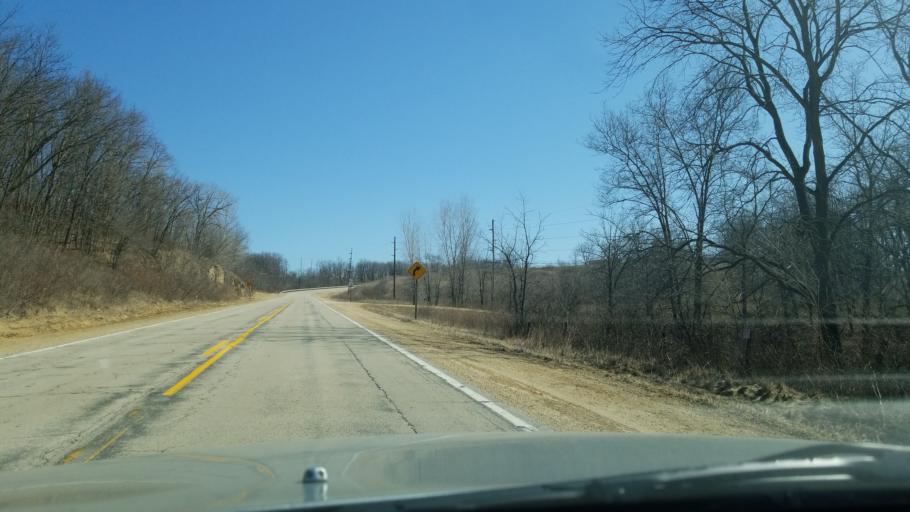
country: US
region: Wisconsin
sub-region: Iowa County
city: Mineral Point
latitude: 42.9042
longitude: -90.2309
